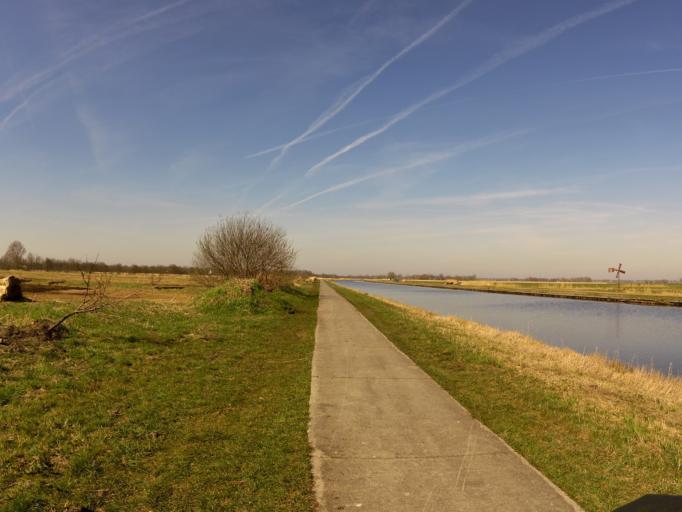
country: NL
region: Overijssel
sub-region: Gemeente Steenwijkerland
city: Oldemarkt
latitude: 52.8017
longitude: 5.9542
